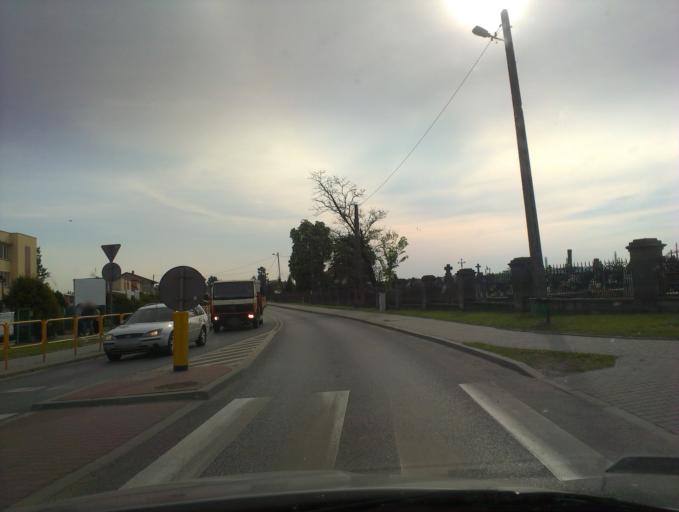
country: PL
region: Swietokrzyskie
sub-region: Powiat ostrowiecki
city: Ostrowiec Swietokrzyski
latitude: 50.9171
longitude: 21.3652
